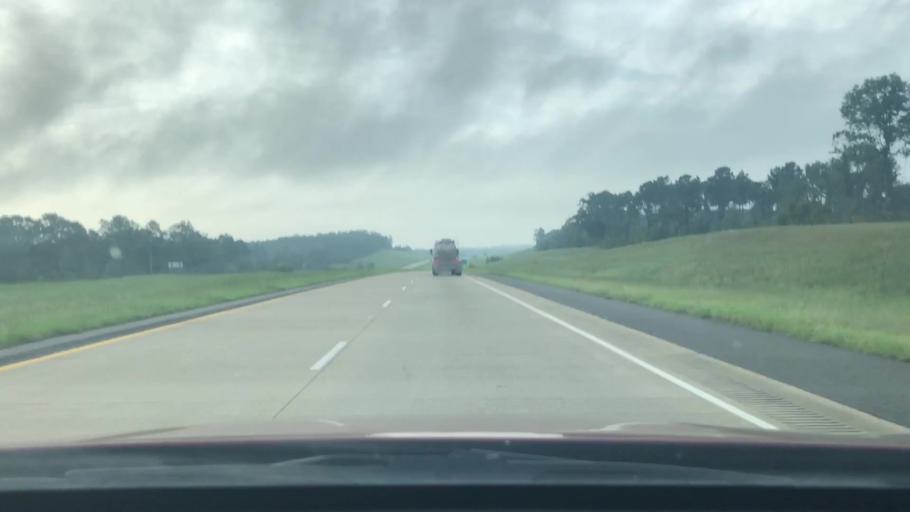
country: US
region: Louisiana
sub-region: Caddo Parish
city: Vivian
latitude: 32.9579
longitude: -93.9023
